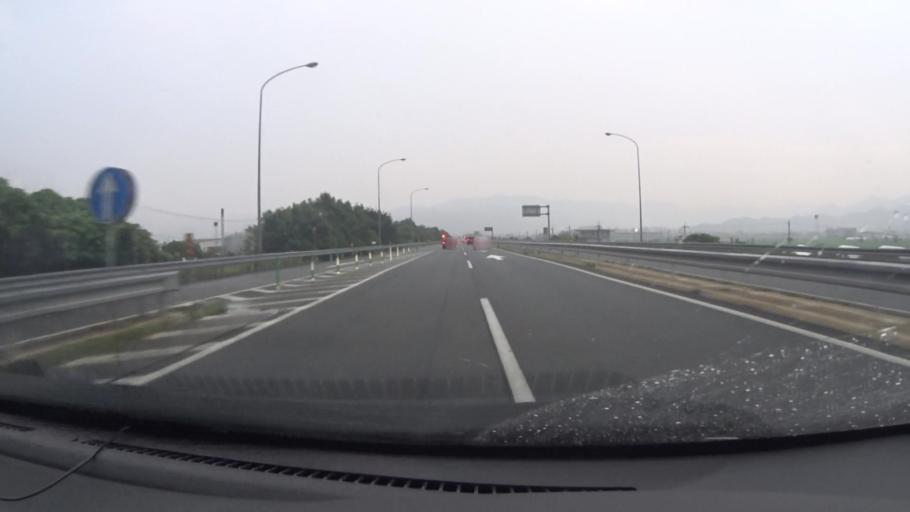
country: JP
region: Kyoto
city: Kameoka
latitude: 35.0295
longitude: 135.5461
